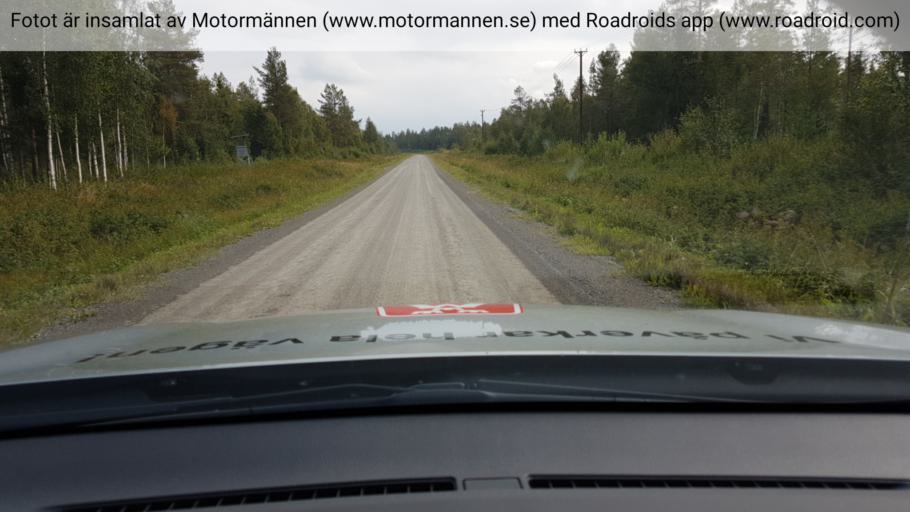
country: SE
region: Jaemtland
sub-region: Stroemsunds Kommun
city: Stroemsund
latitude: 63.7339
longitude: 15.4417
